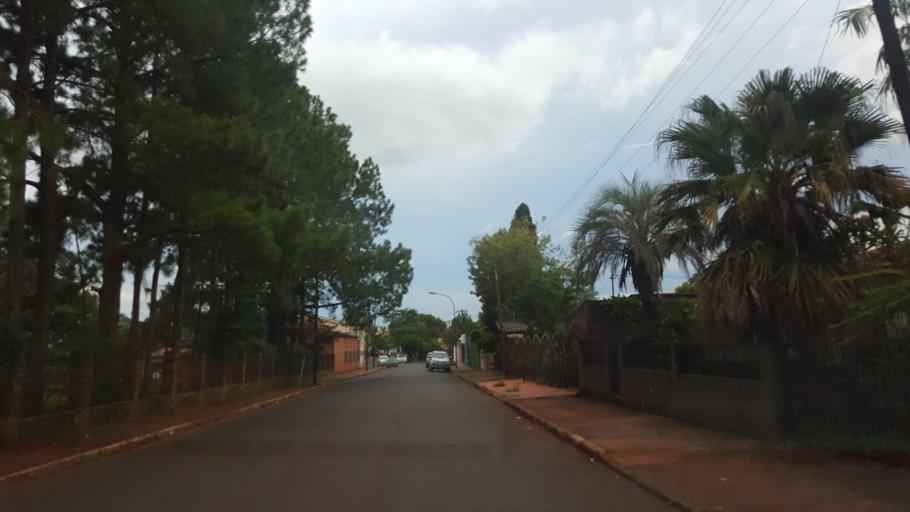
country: AR
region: Misiones
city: Jardin America
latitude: -27.0462
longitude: -55.2337
